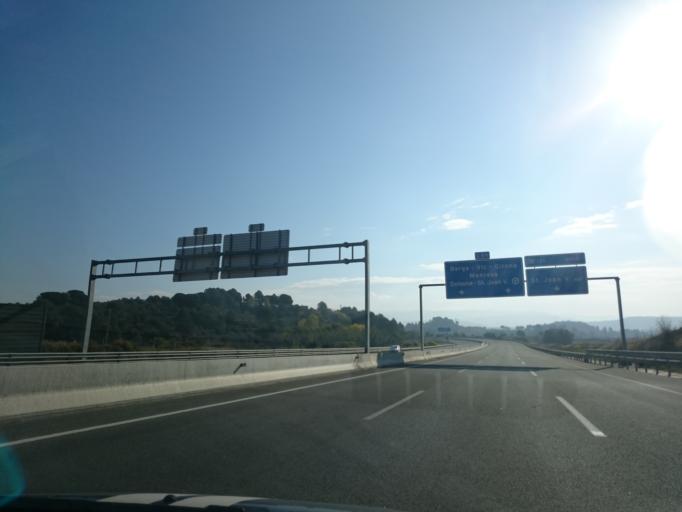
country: ES
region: Catalonia
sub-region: Provincia de Barcelona
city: Sant Joan de Vilatorrada
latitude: 41.7309
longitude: 1.7871
